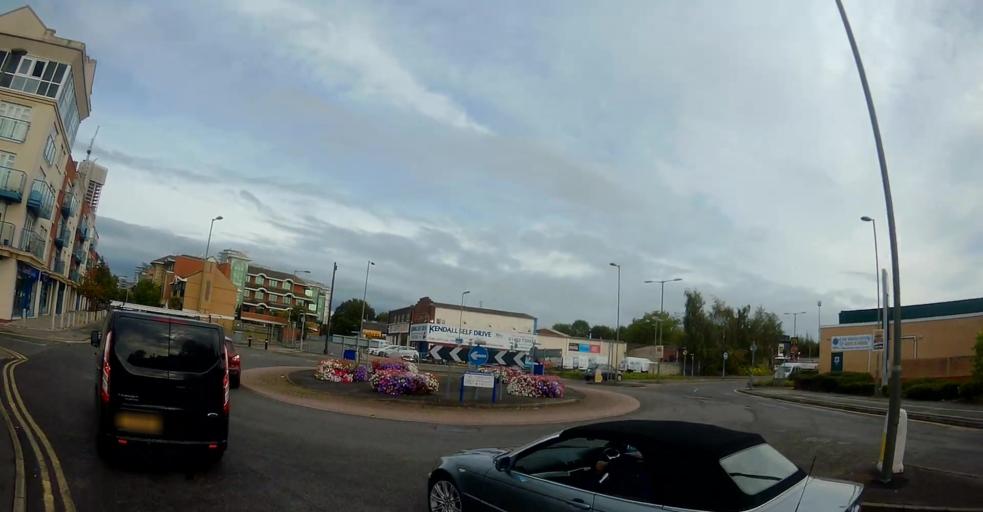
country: GB
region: England
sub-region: Surrey
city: Woking
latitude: 51.3172
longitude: -0.5670
